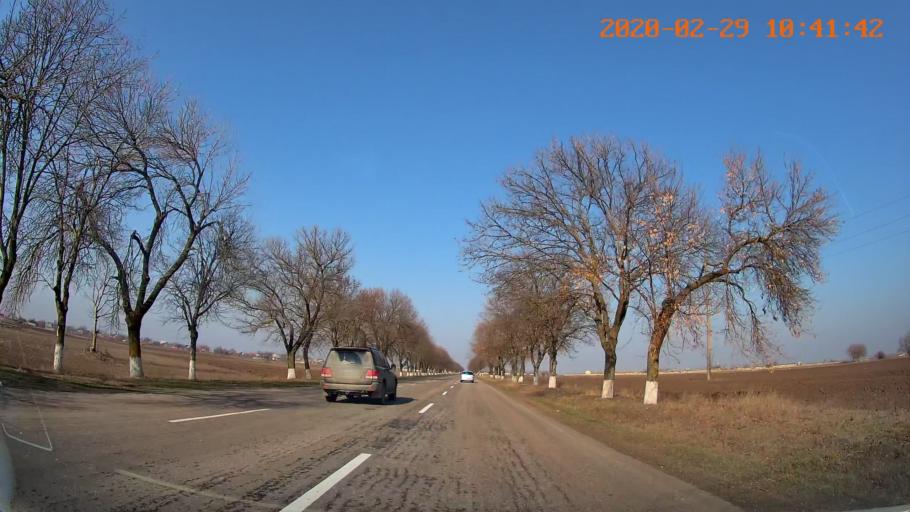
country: MD
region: Telenesti
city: Grigoriopol
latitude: 47.0449
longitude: 29.4214
